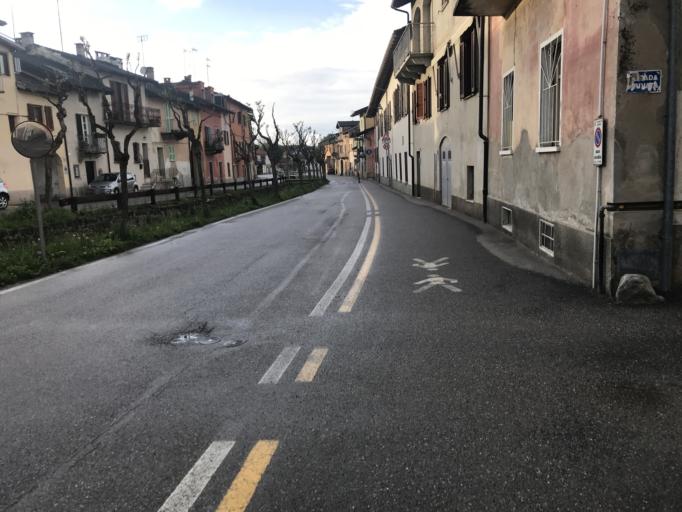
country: IT
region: Piedmont
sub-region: Provincia di Cuneo
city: Boves
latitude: 44.3303
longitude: 7.5470
